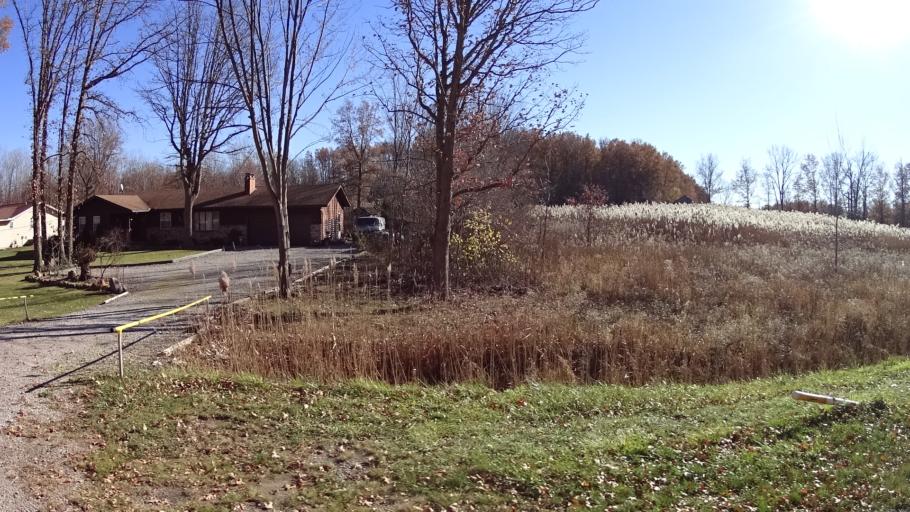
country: US
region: Ohio
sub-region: Lorain County
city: Avon Center
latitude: 41.4650
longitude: -81.9842
